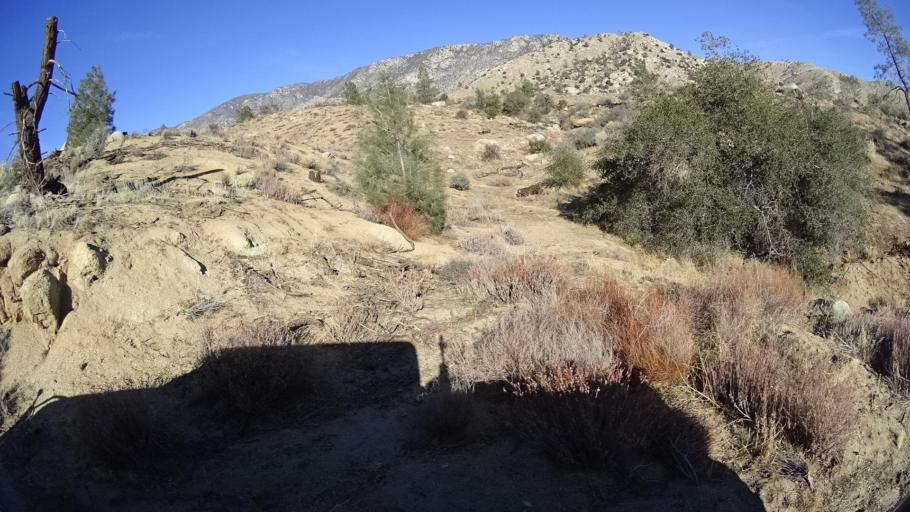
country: US
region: California
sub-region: Kern County
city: Weldon
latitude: 35.7090
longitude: -118.3045
